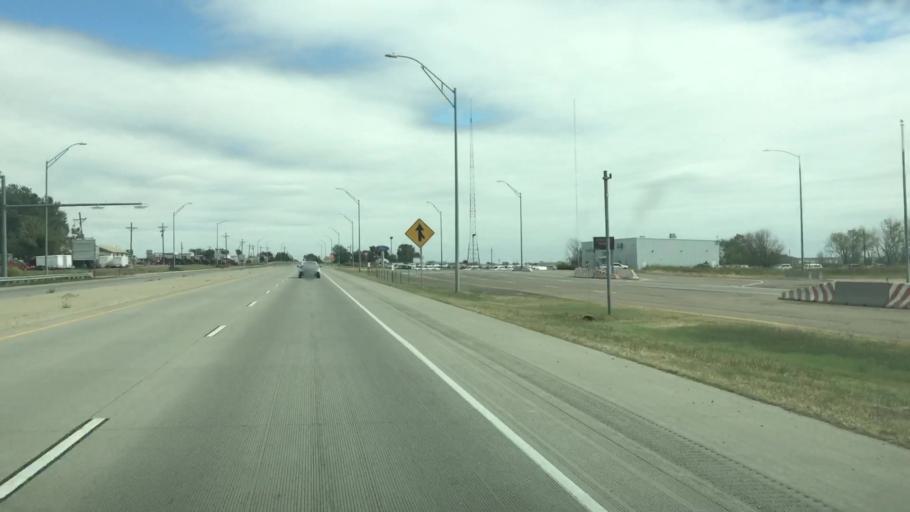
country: US
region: Colorado
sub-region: Prowers County
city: Lamar
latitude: 38.1146
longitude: -102.6278
